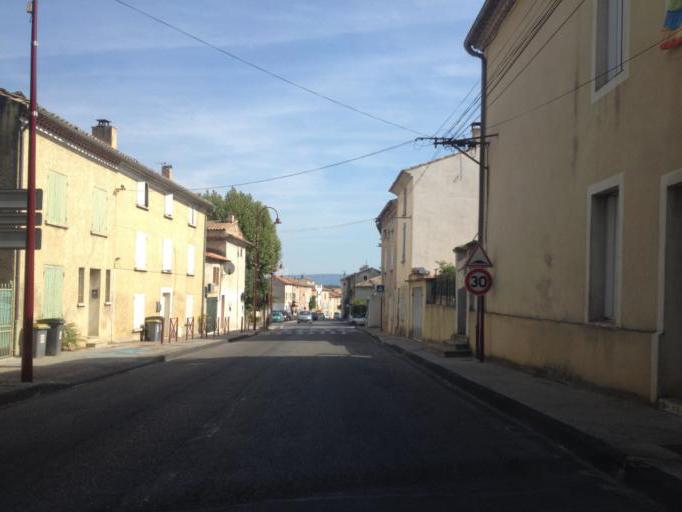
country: FR
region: Provence-Alpes-Cote d'Azur
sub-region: Departement du Vaucluse
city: Aubignan
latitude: 44.1017
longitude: 5.0242
